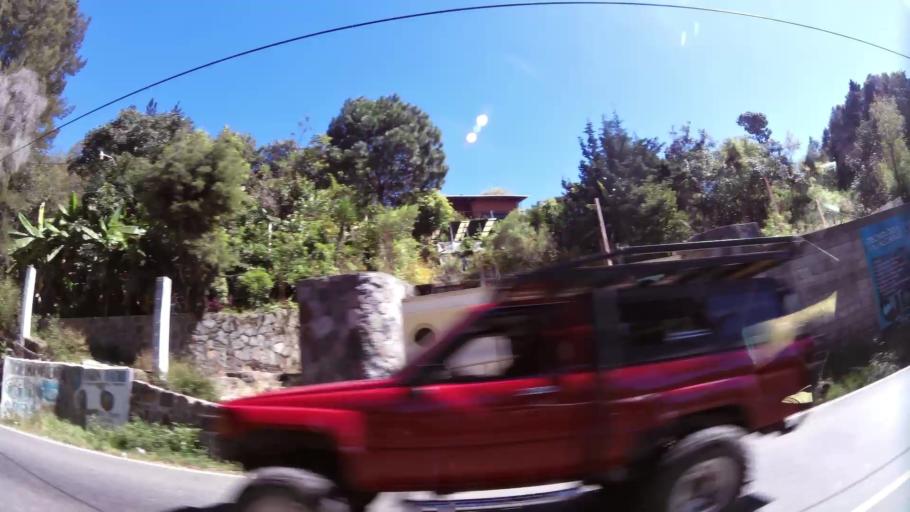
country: GT
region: Solola
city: Solola
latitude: 14.7631
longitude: -91.1773
